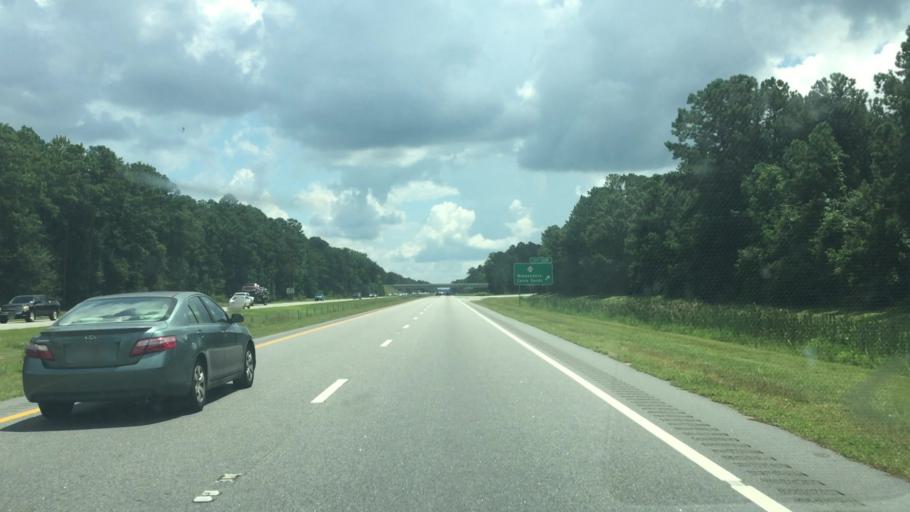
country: US
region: North Carolina
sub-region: Columbus County
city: Chadbourn
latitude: 34.3993
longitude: -78.9084
